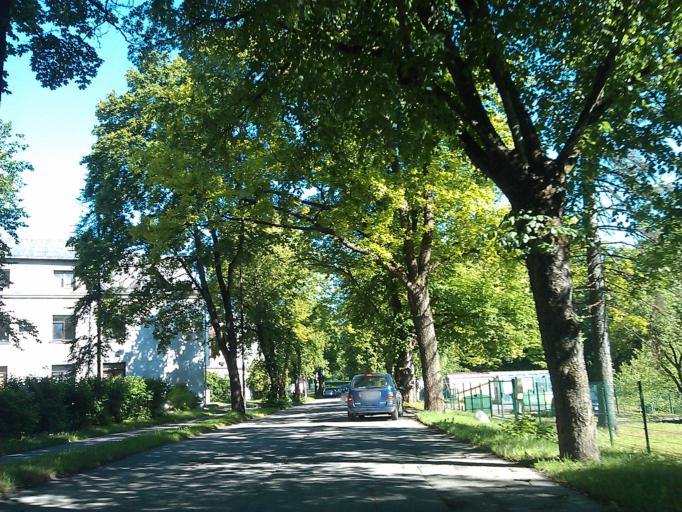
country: LV
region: Cesu Rajons
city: Cesis
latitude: 57.3091
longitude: 25.2502
